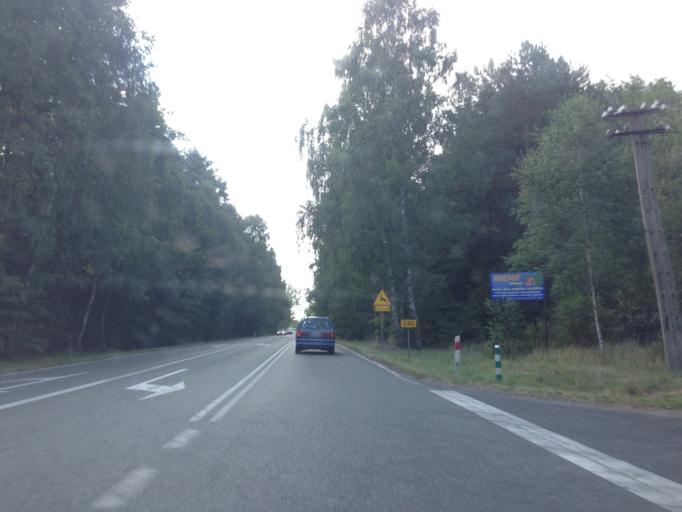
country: PL
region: Kujawsko-Pomorskie
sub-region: Powiat swiecki
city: Swiekatowo
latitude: 53.4751
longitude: 18.1522
